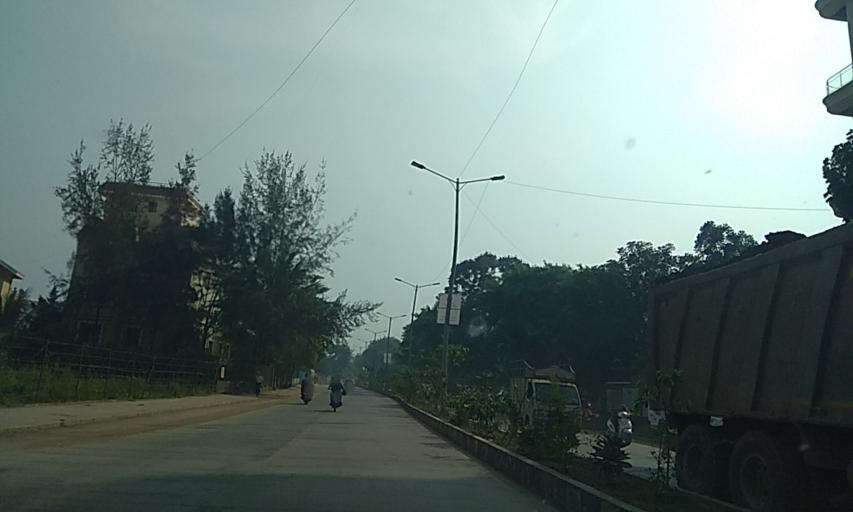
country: IN
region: Maharashtra
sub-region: Pune Division
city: Pimpri
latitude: 18.5599
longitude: 73.7820
